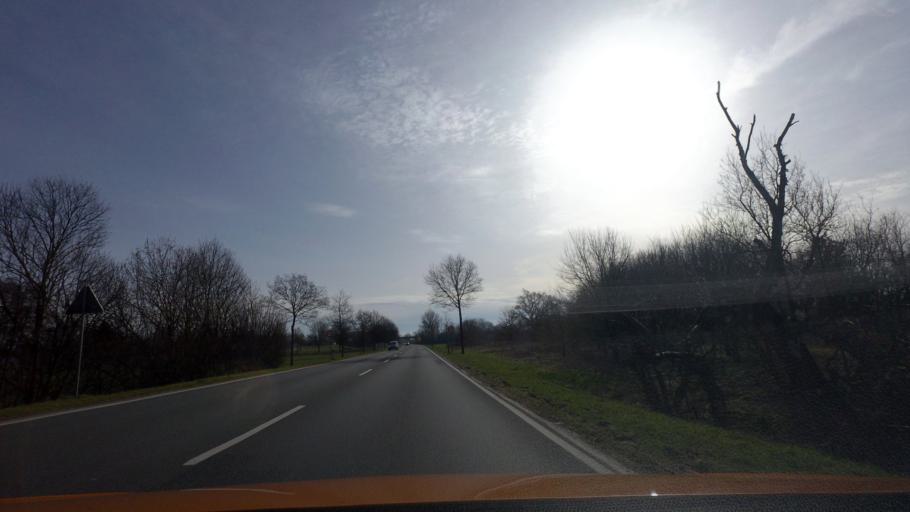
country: DE
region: Lower Saxony
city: Sulingen
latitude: 52.6706
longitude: 8.7991
